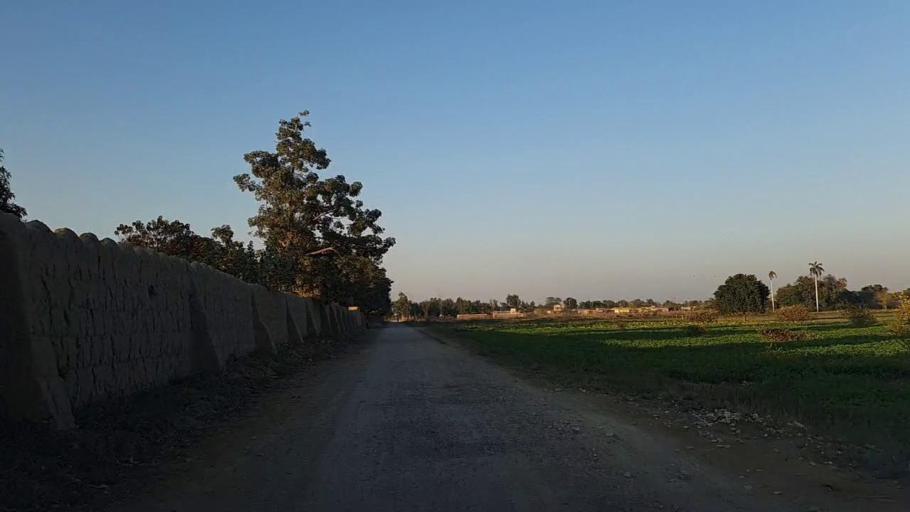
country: PK
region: Sindh
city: Nawabshah
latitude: 26.2440
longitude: 68.3383
